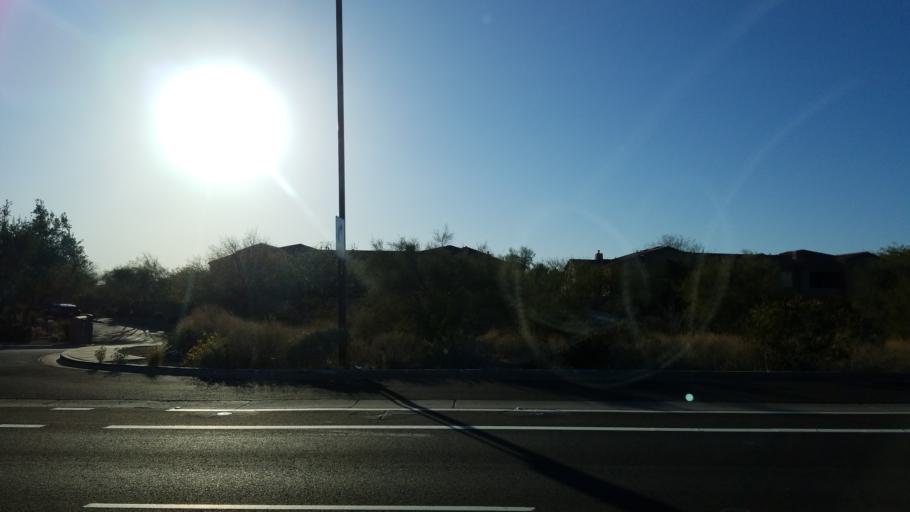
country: US
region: Arizona
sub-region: Maricopa County
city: Paradise Valley
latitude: 33.6664
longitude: -111.8907
